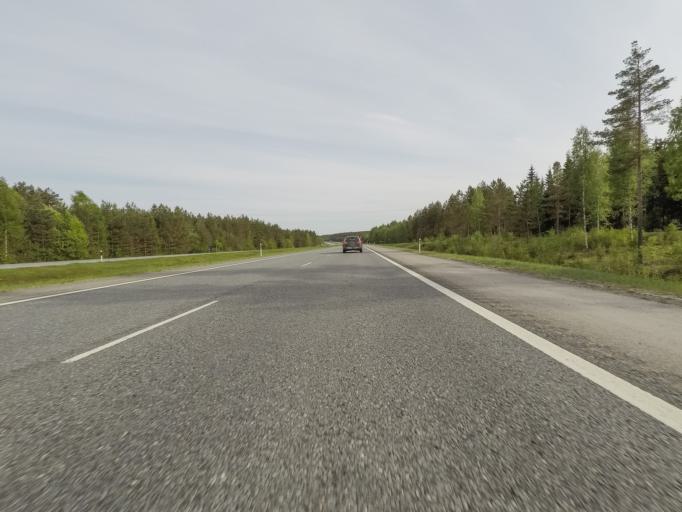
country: FI
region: Haeme
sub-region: Haemeenlinna
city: Haemeenlinna
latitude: 60.9372
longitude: 24.5149
